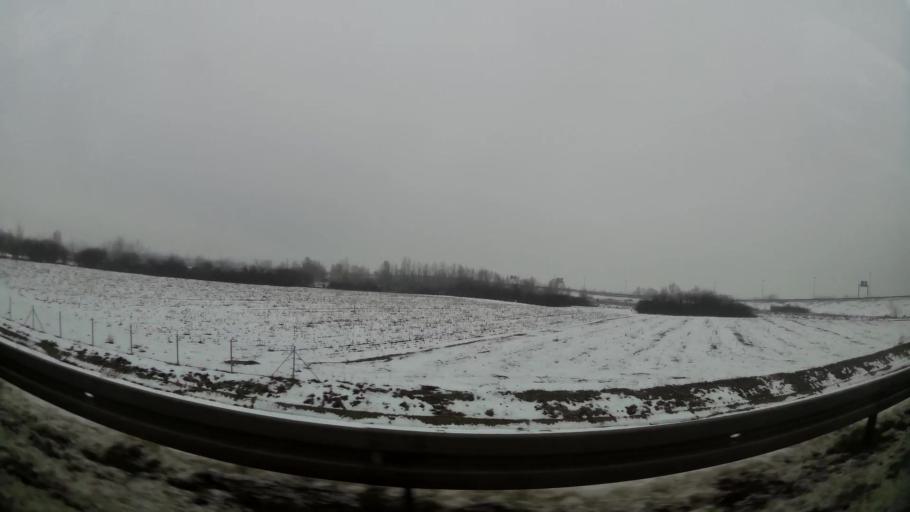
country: RS
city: Ostruznica
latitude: 44.7341
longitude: 20.3337
